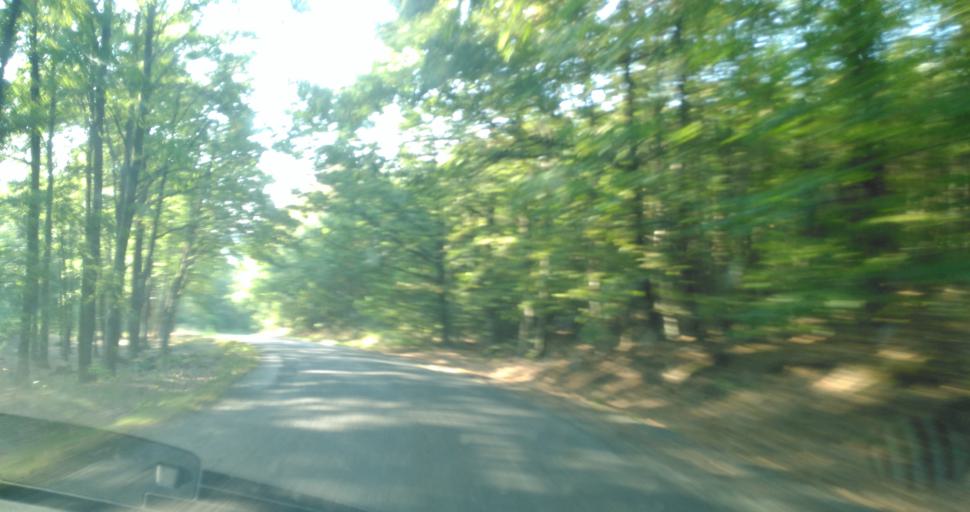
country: CZ
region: Central Bohemia
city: Roztoky
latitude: 49.9786
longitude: 13.8687
